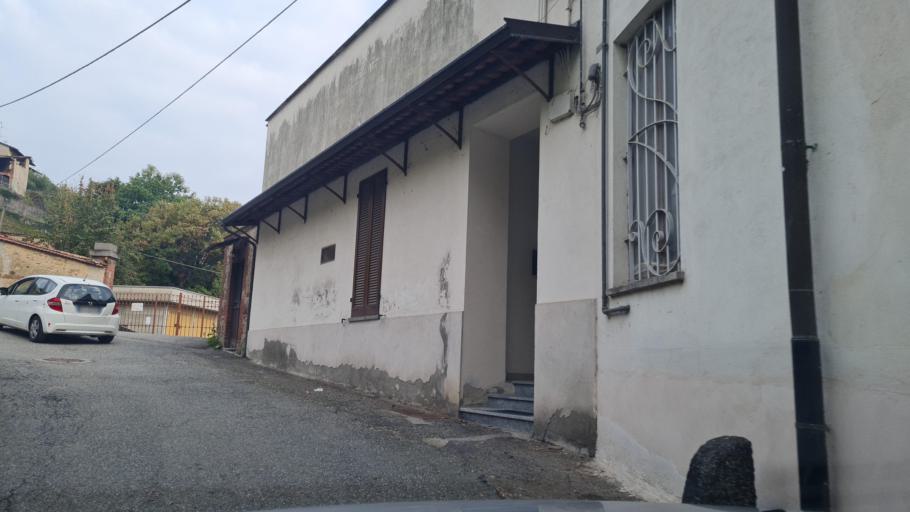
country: IT
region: Piedmont
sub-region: Provincia di Biella
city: Occhieppo Superiore
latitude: 45.5625
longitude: 8.0033
